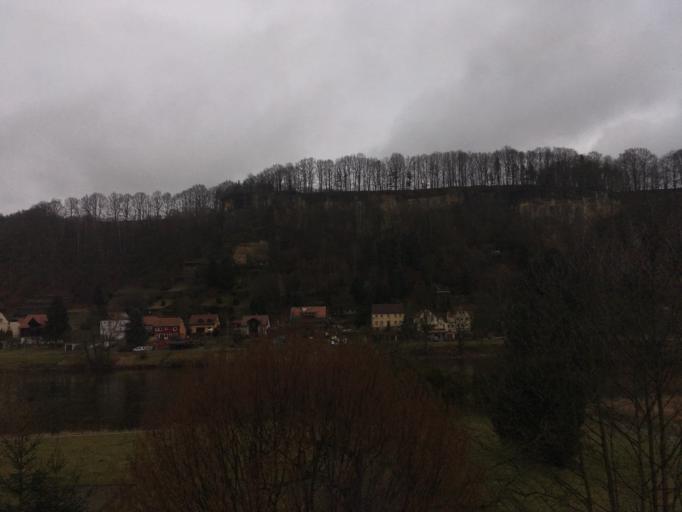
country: DE
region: Saxony
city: Struppen
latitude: 50.9512
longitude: 13.9853
